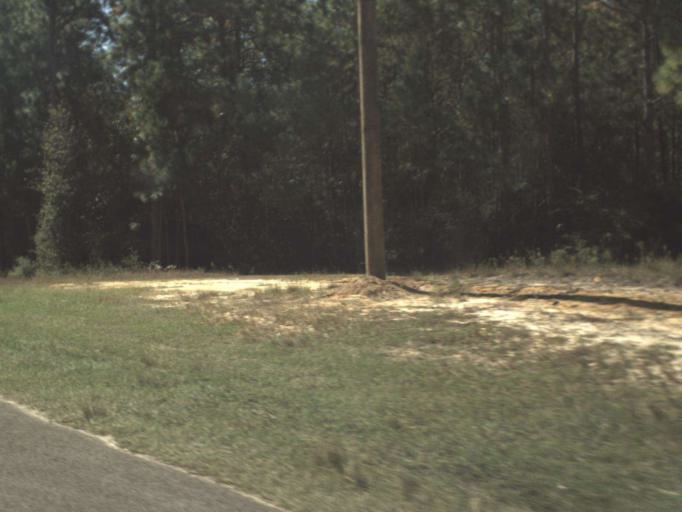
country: US
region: Florida
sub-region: Walton County
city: DeFuniak Springs
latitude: 30.8835
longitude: -86.1254
